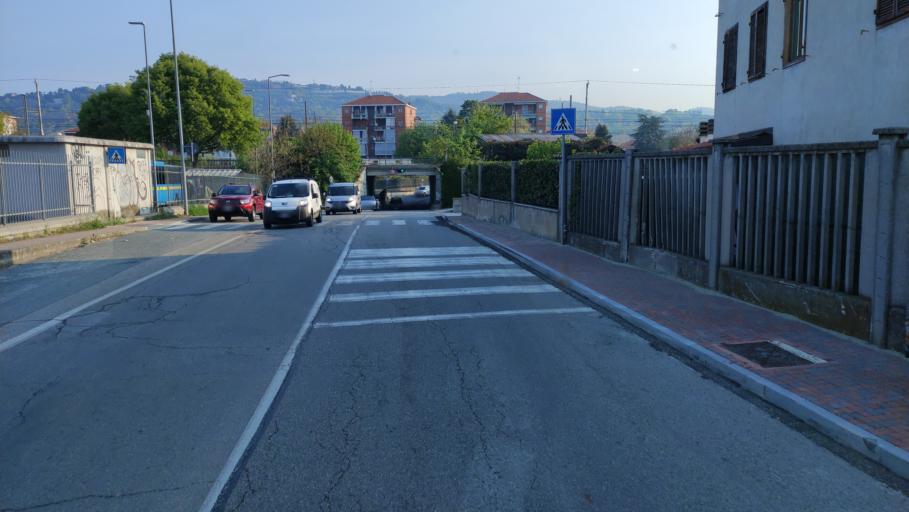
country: IT
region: Piedmont
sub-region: Provincia di Torino
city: Moncalieri
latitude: 44.9912
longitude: 7.7052
